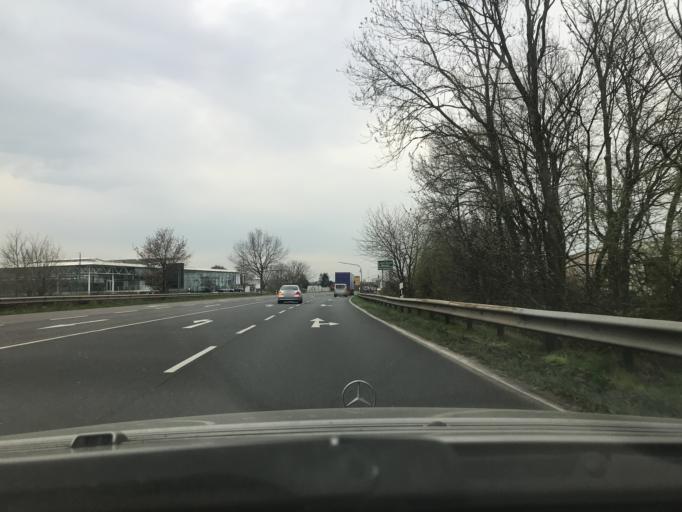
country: DE
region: North Rhine-Westphalia
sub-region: Regierungsbezirk Dusseldorf
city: Korschenbroich
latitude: 51.2225
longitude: 6.4859
